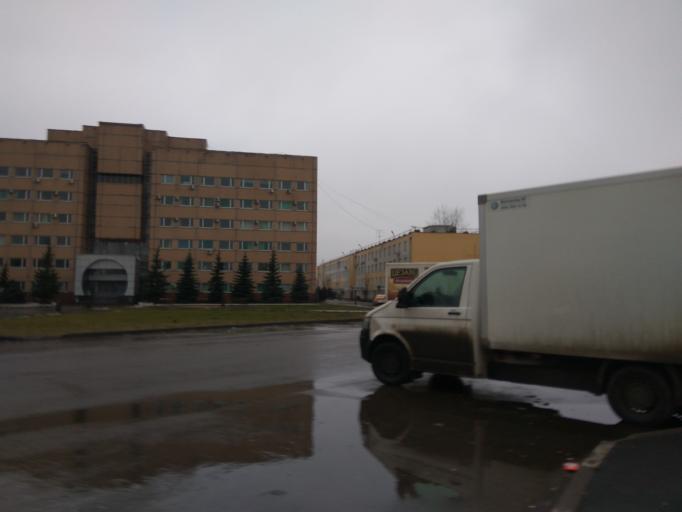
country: RU
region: Moscow
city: Tekstil'shchiki
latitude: 55.7055
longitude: 37.7270
